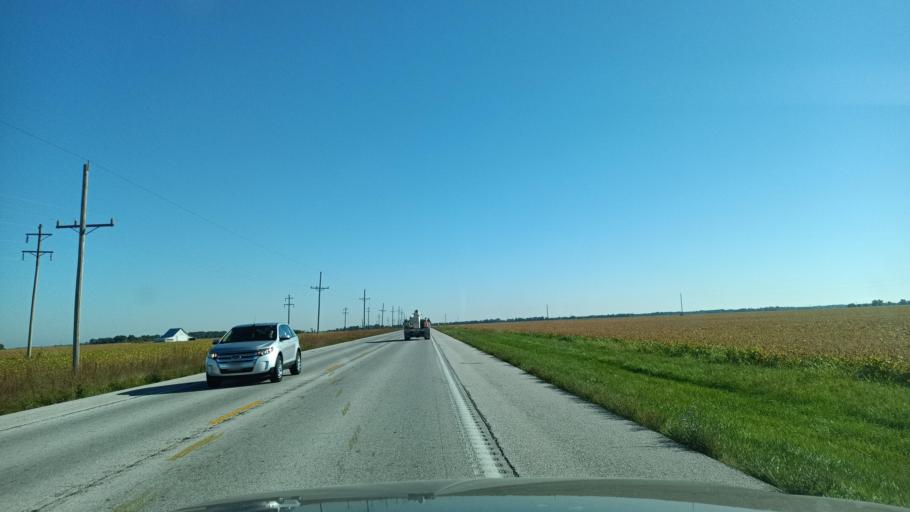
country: US
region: Missouri
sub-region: Audrain County
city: Vandalia
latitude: 39.4742
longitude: -91.5897
